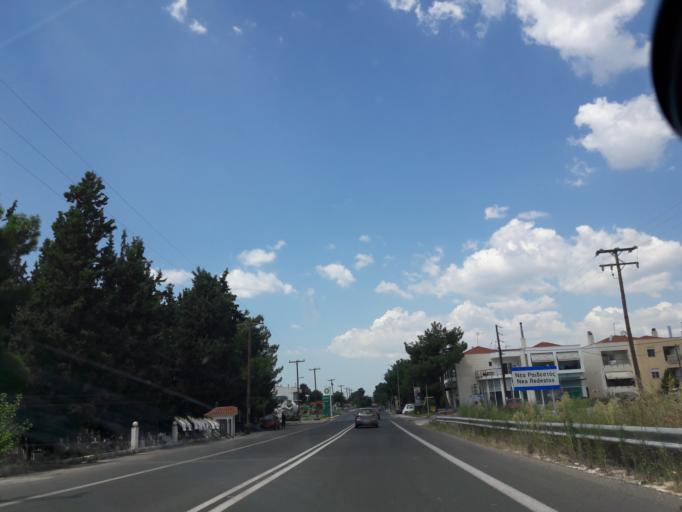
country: GR
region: Central Macedonia
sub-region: Nomos Thessalonikis
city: Agia Paraskevi
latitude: 40.5215
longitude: 23.0566
